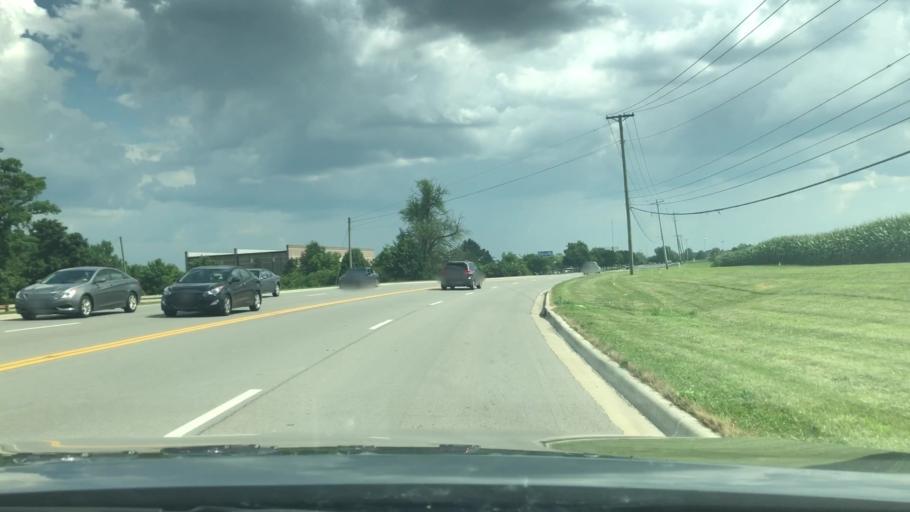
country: US
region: Ohio
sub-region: Franklin County
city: Upper Arlington
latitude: 40.0174
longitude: -83.0377
